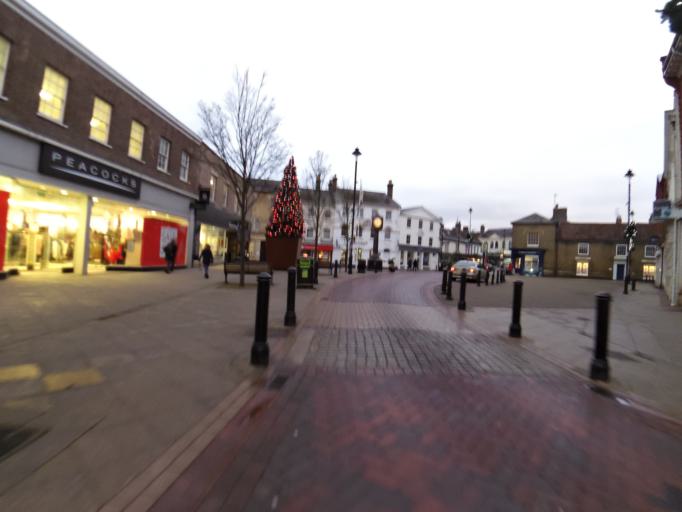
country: GB
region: England
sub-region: Suffolk
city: Stowmarket
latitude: 52.1875
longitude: 0.9958
